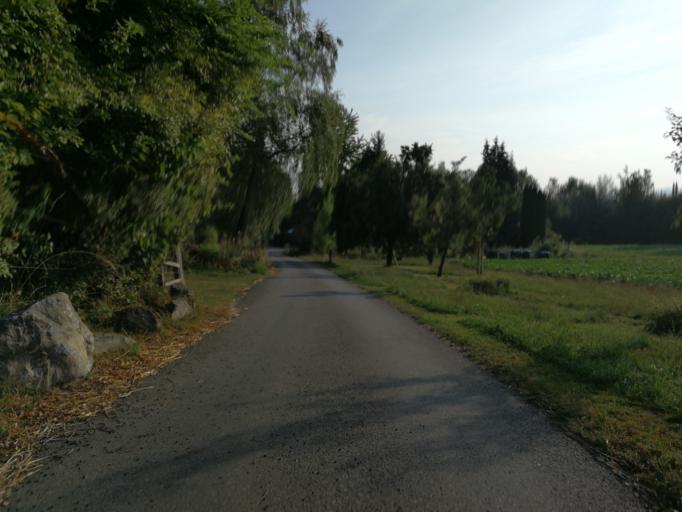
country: CH
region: Zurich
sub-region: Bezirk Uster
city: Esslingen
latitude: 47.2822
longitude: 8.7200
